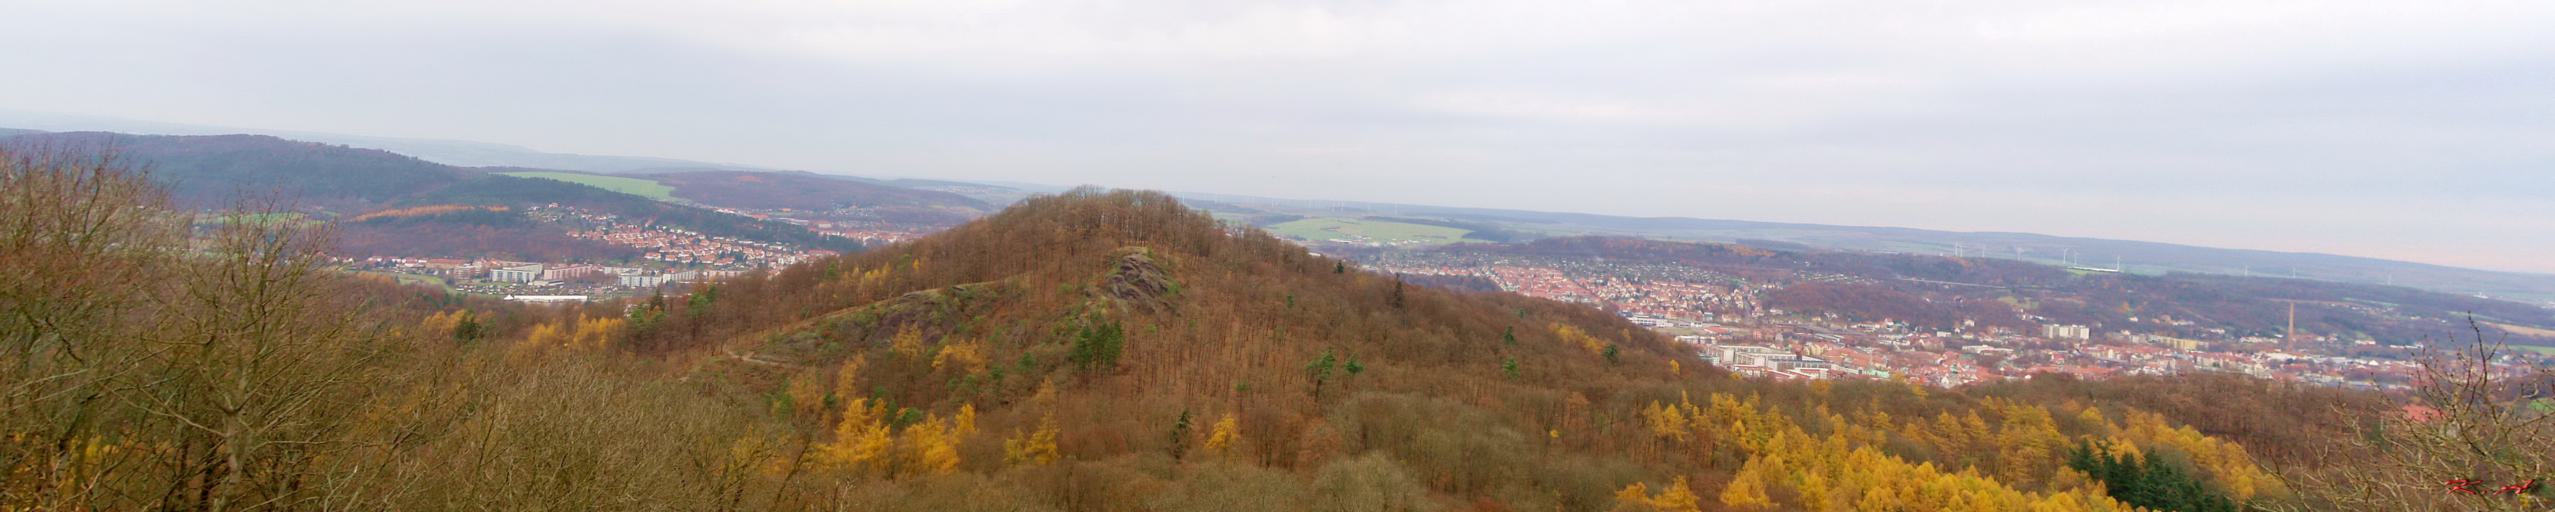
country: DE
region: Thuringia
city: Eisenach
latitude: 50.9669
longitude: 10.3071
